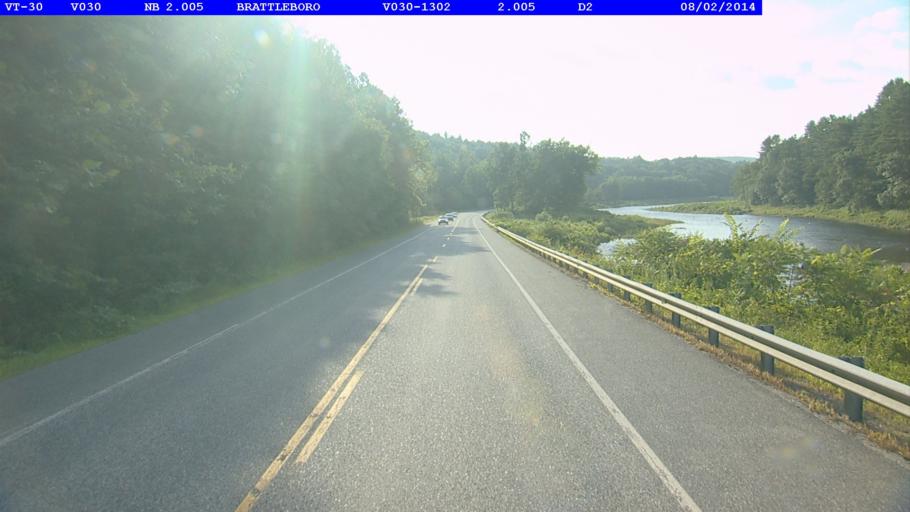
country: US
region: Vermont
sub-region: Windham County
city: West Brattleboro
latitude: 42.8807
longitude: -72.5810
